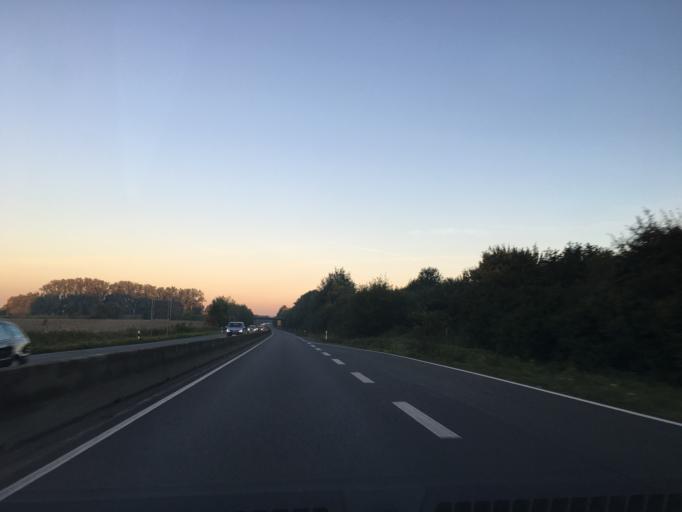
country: DE
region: North Rhine-Westphalia
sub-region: Regierungsbezirk Munster
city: Altenberge
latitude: 52.0365
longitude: 7.4686
